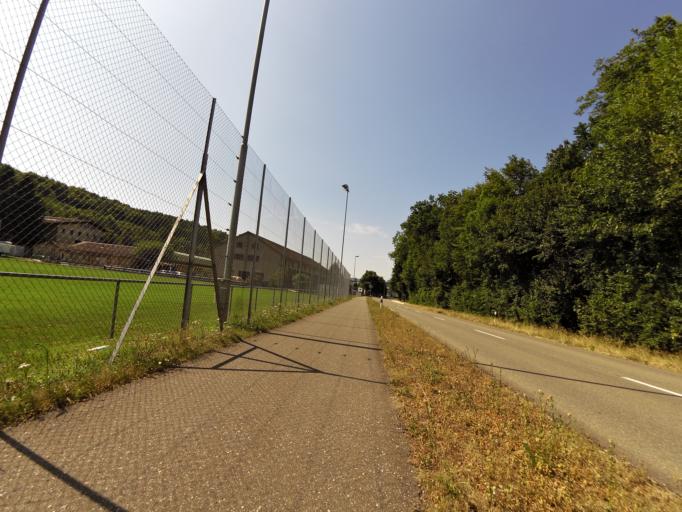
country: CH
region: Aargau
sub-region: Bezirk Brugg
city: Windisch
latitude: 47.4712
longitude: 8.2282
